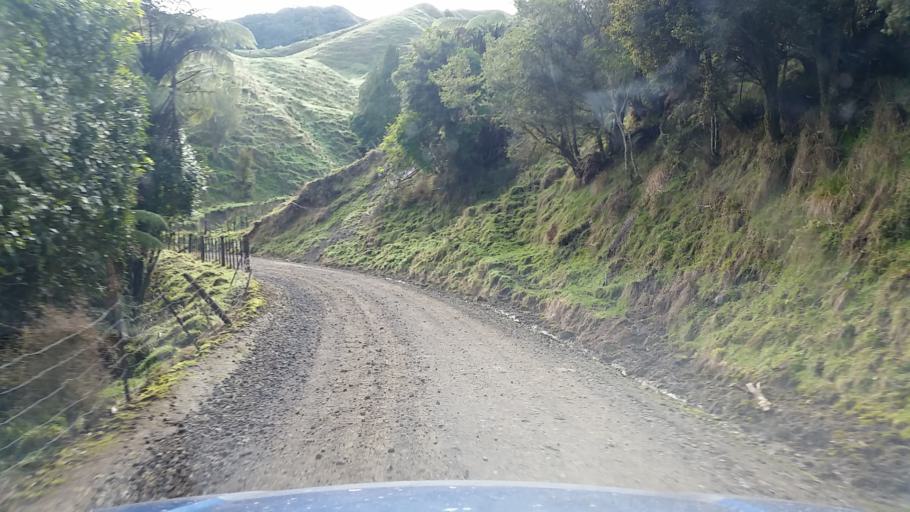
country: NZ
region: Taranaki
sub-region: New Plymouth District
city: Waitara
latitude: -39.1055
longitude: 174.8460
